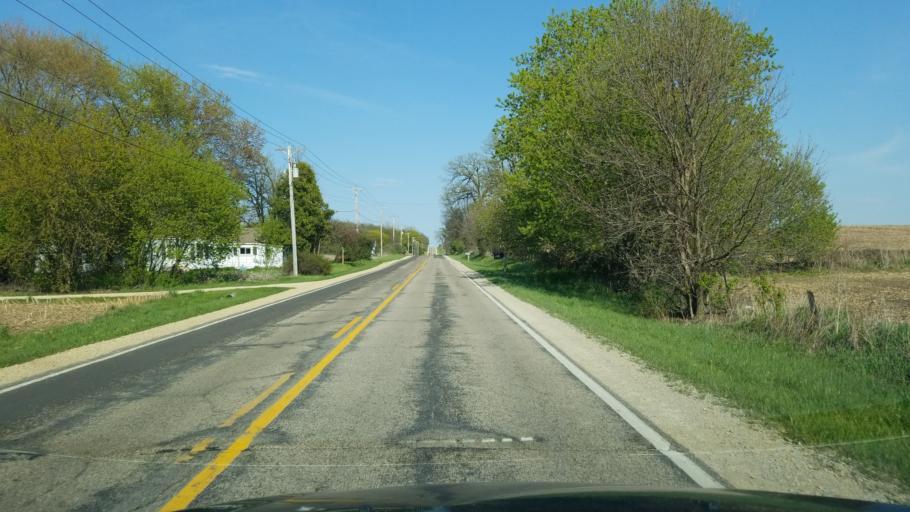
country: US
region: Wisconsin
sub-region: Dane County
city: Oregon
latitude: 42.9290
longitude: -89.4288
